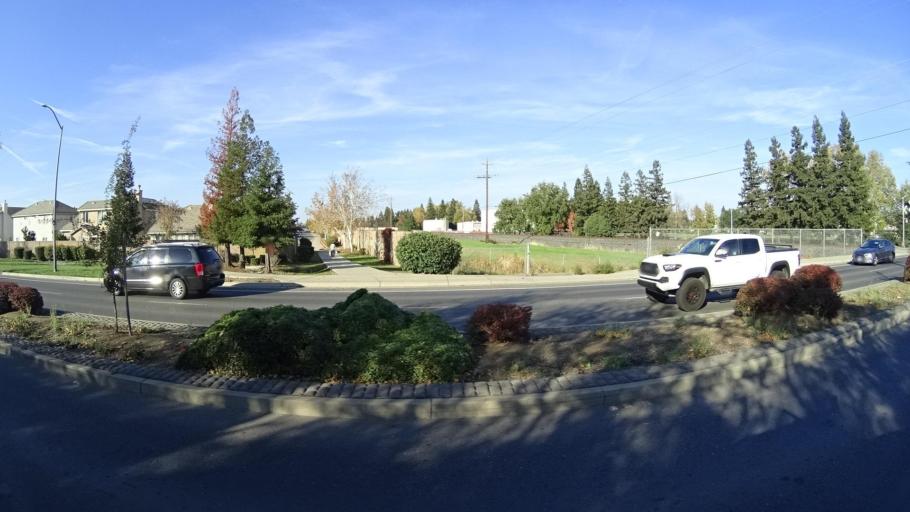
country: US
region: California
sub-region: Sacramento County
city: Vineyard
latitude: 38.4525
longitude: -121.3813
